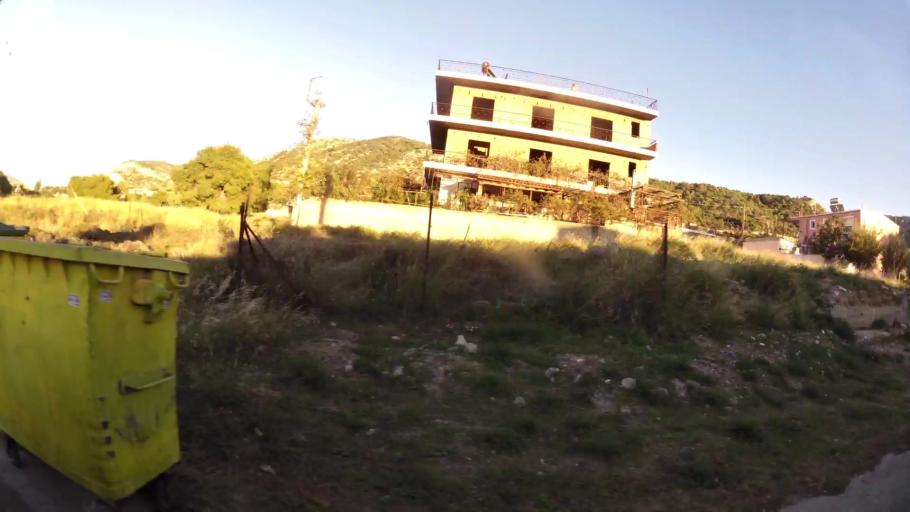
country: GR
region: Attica
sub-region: Nomarchia Athinas
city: Chaidari
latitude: 38.0402
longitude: 23.6371
